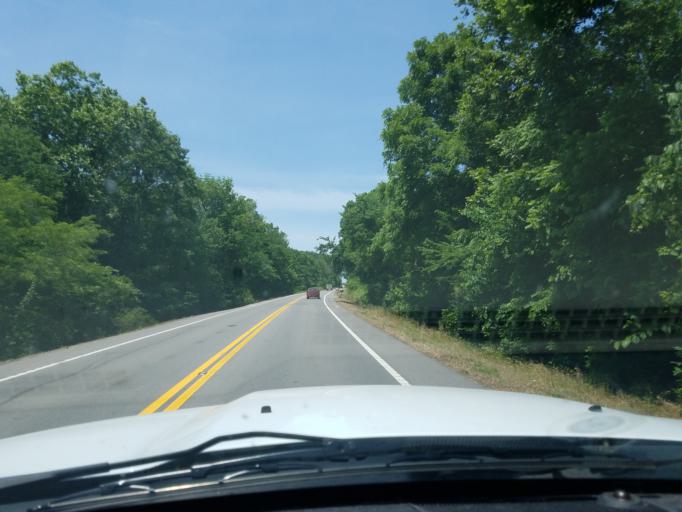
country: US
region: Tennessee
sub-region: Sumner County
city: Westmoreland
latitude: 36.4657
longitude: -86.2699
